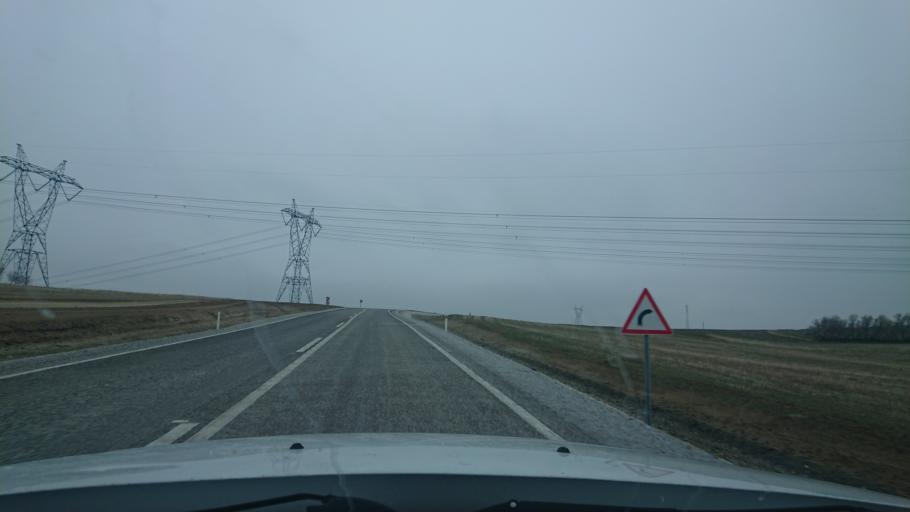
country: TR
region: Aksaray
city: Agacoren
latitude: 38.8988
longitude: 33.9323
